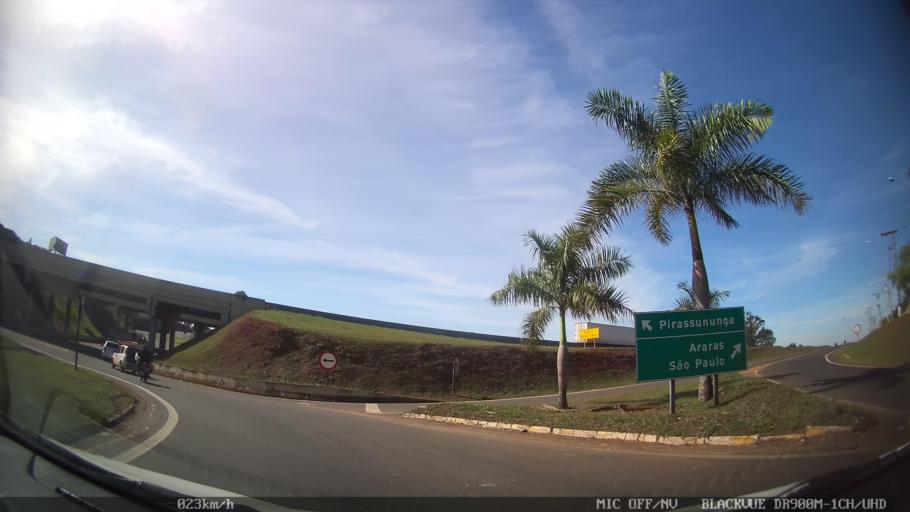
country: BR
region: Sao Paulo
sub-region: Leme
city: Leme
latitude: -22.2034
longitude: -47.3960
